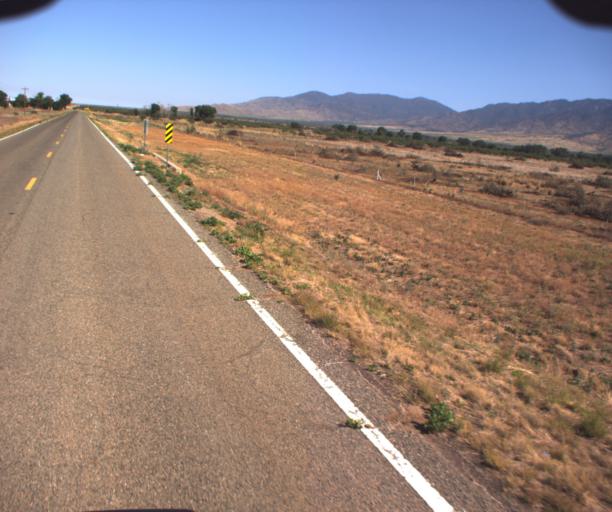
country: US
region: Arizona
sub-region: Graham County
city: Swift Trail Junction
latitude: 32.5863
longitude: -109.9640
